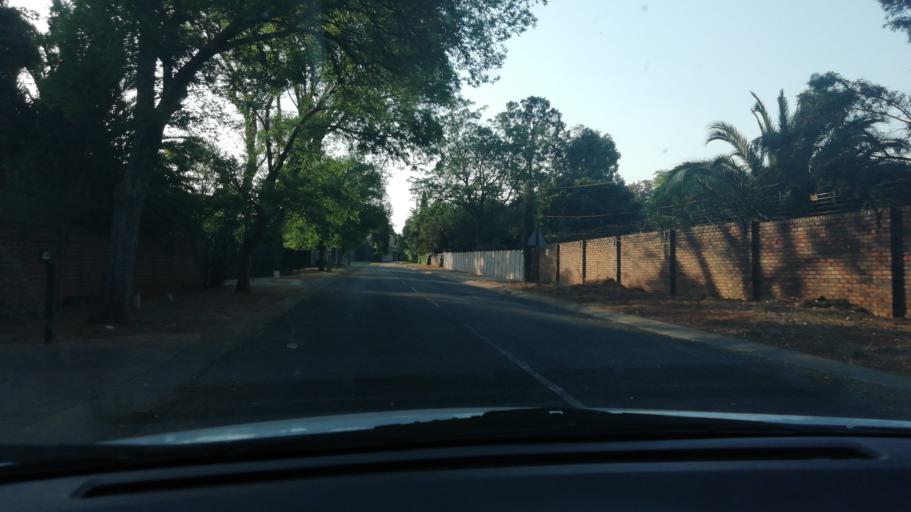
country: ZA
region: Gauteng
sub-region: Ekurhuleni Metropolitan Municipality
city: Benoni
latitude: -26.1972
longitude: 28.2893
